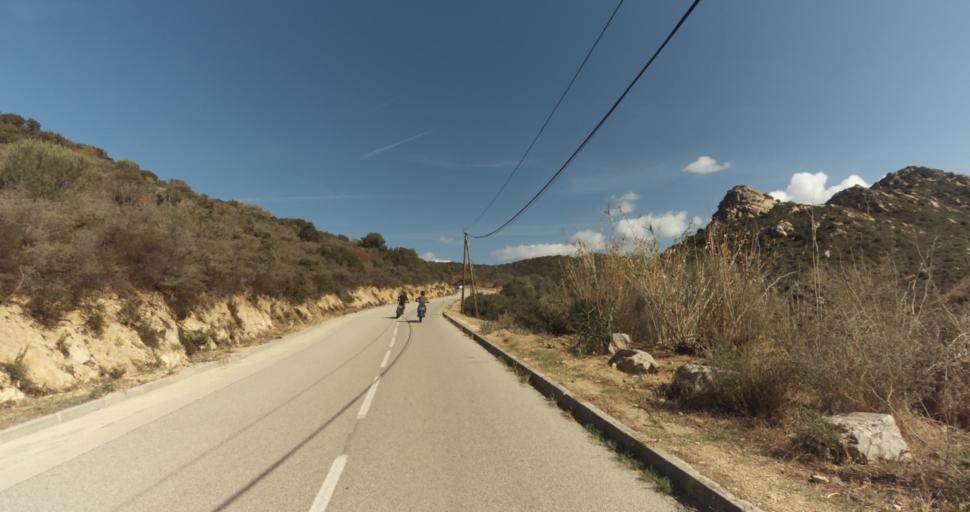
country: FR
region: Corsica
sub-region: Departement de la Corse-du-Sud
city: Ajaccio
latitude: 41.9146
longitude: 8.6439
